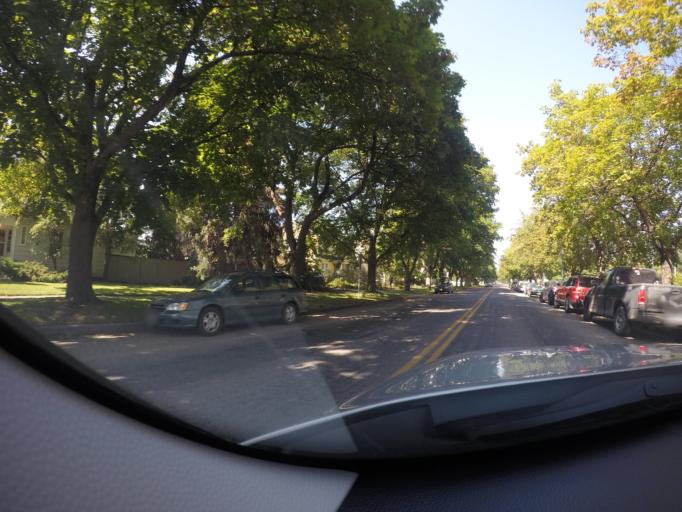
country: US
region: Montana
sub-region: Missoula County
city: Missoula
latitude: 46.8571
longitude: -113.9872
